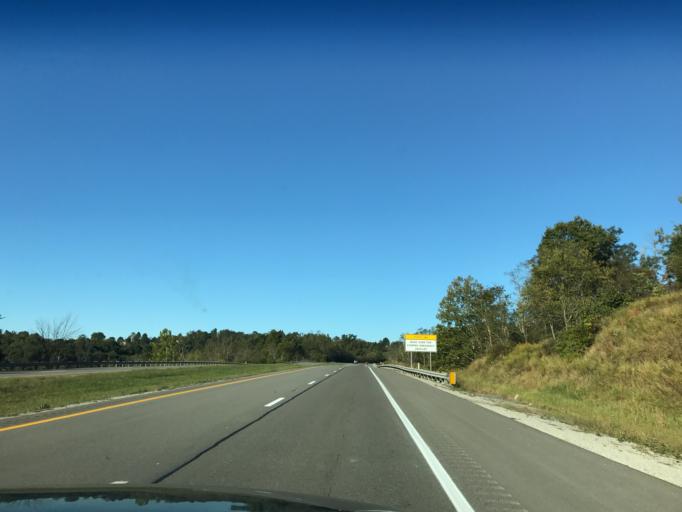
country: US
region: West Virginia
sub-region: Wood County
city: Mineral Wells
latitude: 39.2391
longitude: -81.4509
